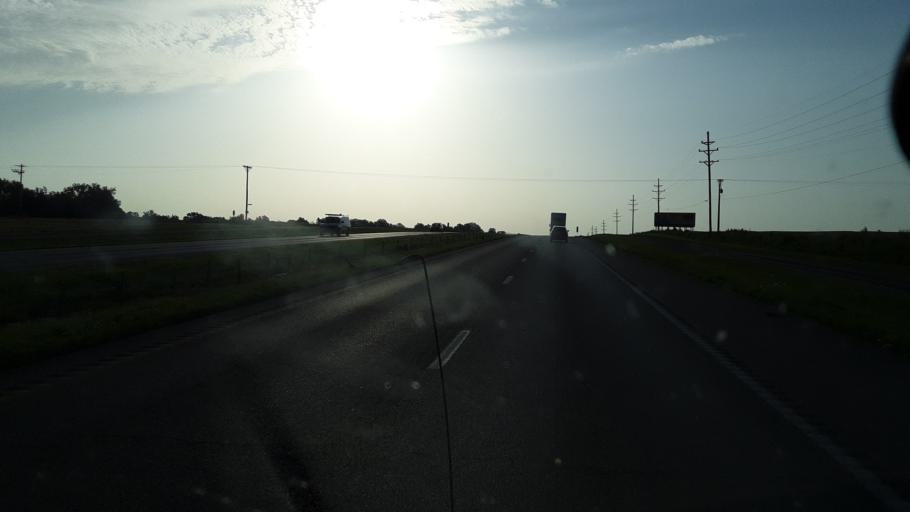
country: US
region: Missouri
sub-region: Warren County
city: Warrenton
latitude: 38.8458
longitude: -91.2567
